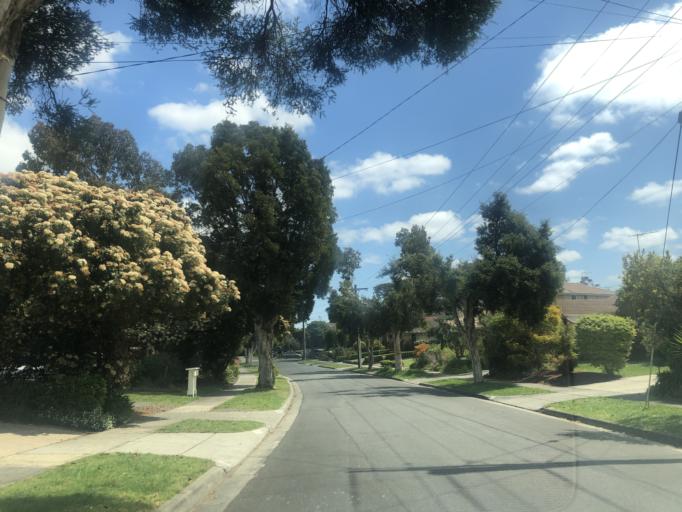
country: AU
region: Victoria
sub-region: Monash
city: Mulgrave
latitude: -37.9104
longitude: 145.1859
